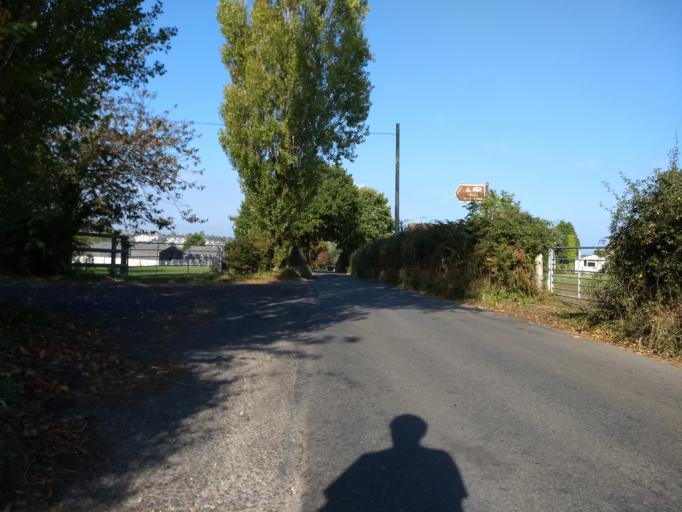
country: GB
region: England
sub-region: Isle of Wight
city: Newchurch
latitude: 50.7231
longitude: -1.2203
